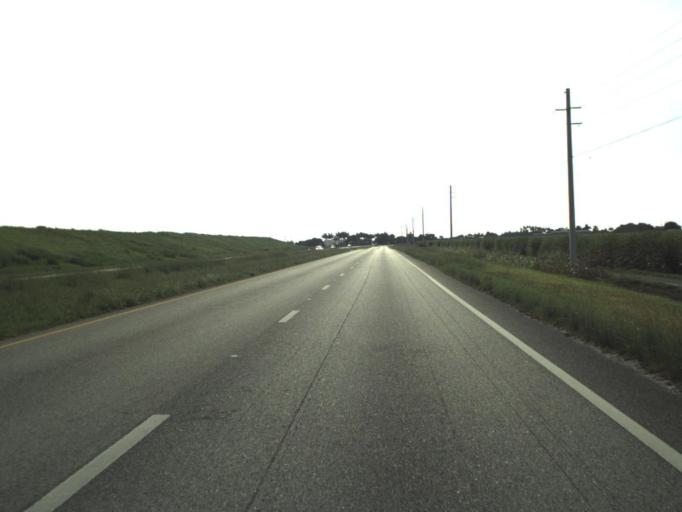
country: US
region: Florida
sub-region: Palm Beach County
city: South Bay
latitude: 26.6805
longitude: -80.7403
